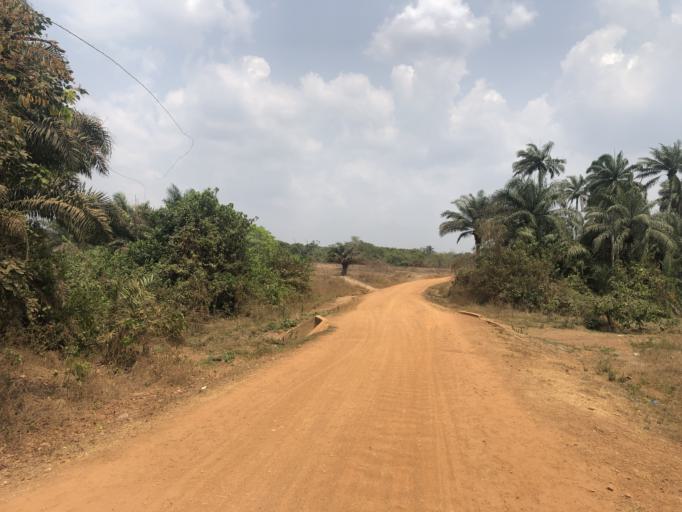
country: NG
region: Osun
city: Bode Osi
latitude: 7.7534
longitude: 4.2355
